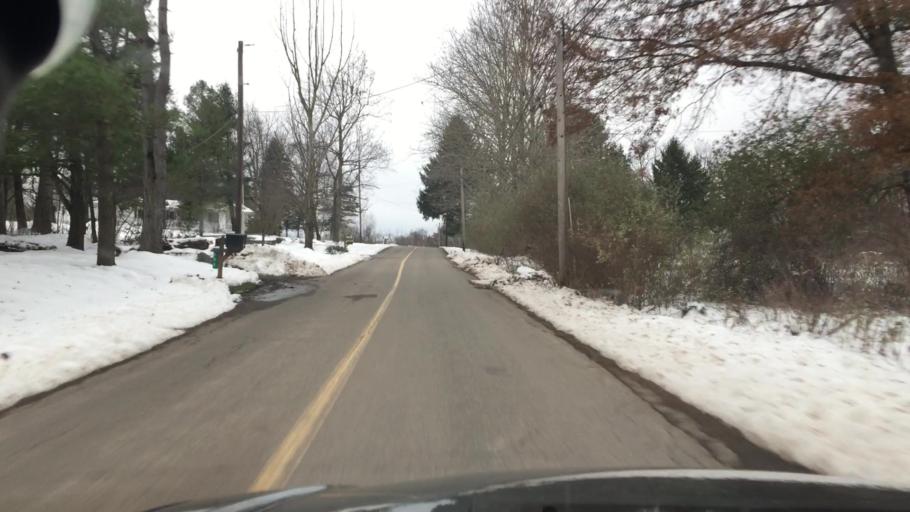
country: US
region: Pennsylvania
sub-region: Luzerne County
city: Conyngham
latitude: 41.0036
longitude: -76.1419
